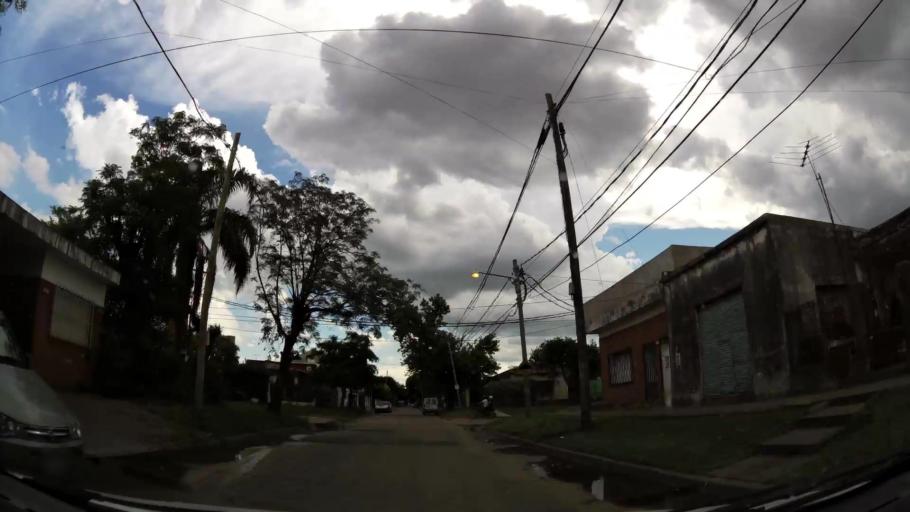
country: AR
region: Buenos Aires
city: Ituzaingo
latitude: -34.6409
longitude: -58.6779
